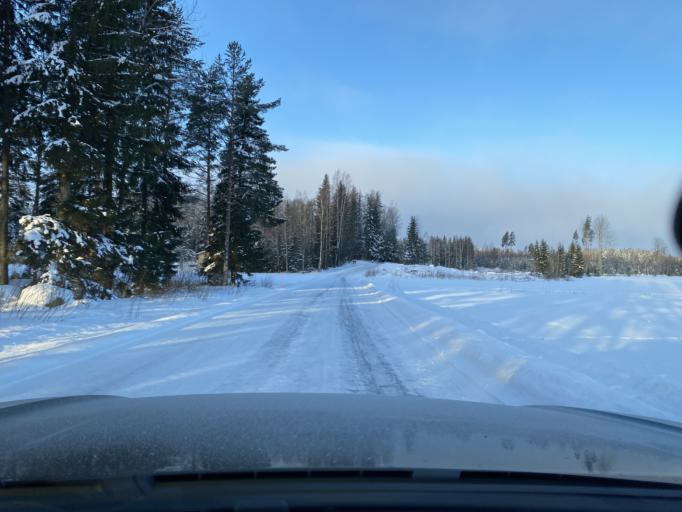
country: FI
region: Haeme
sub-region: Forssa
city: Tammela
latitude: 60.8593
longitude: 23.9058
